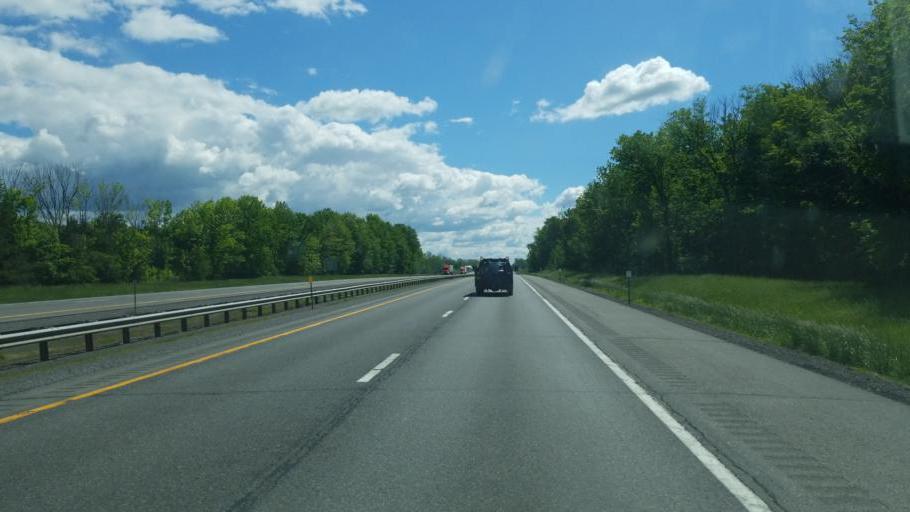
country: US
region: New York
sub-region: Oneida County
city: Vernon
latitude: 43.1263
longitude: -75.5615
